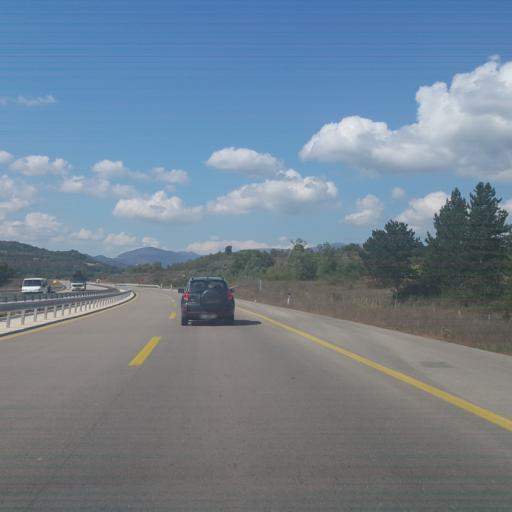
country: RS
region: Central Serbia
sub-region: Pirotski Okrug
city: Bela Palanka
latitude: 43.2464
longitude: 22.2788
